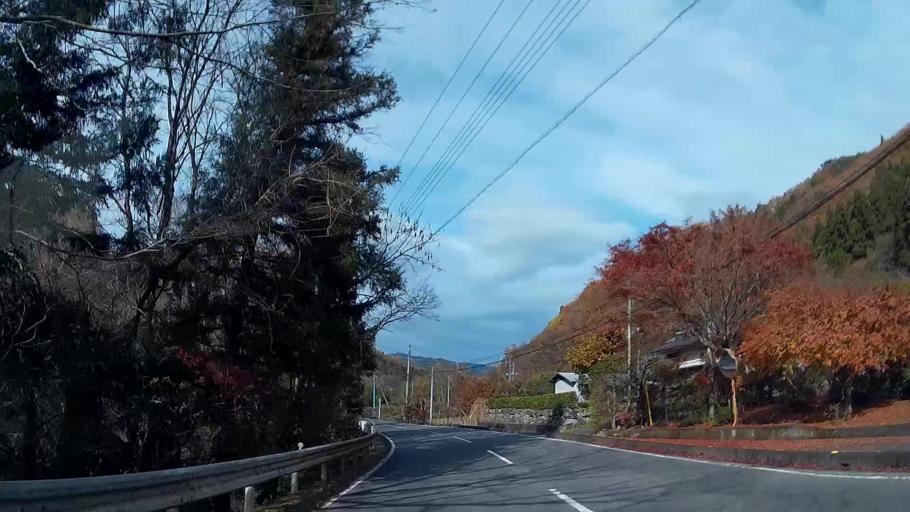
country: JP
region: Saitama
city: Chichibu
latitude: 36.0520
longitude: 138.9827
